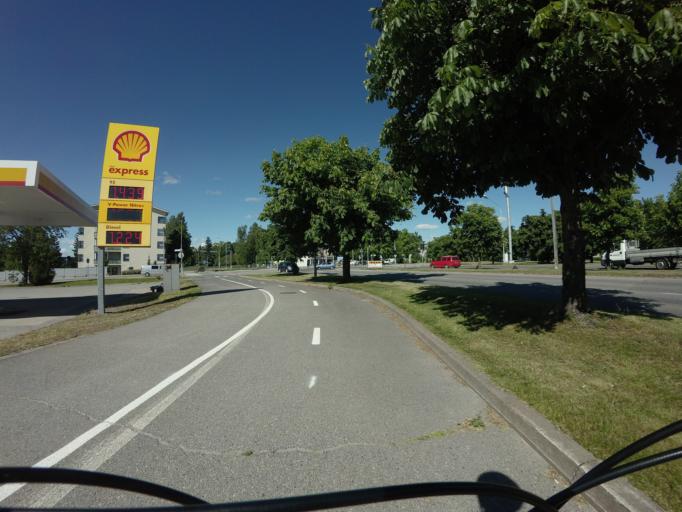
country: FI
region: Varsinais-Suomi
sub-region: Turku
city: Turku
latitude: 60.4638
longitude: 22.2700
